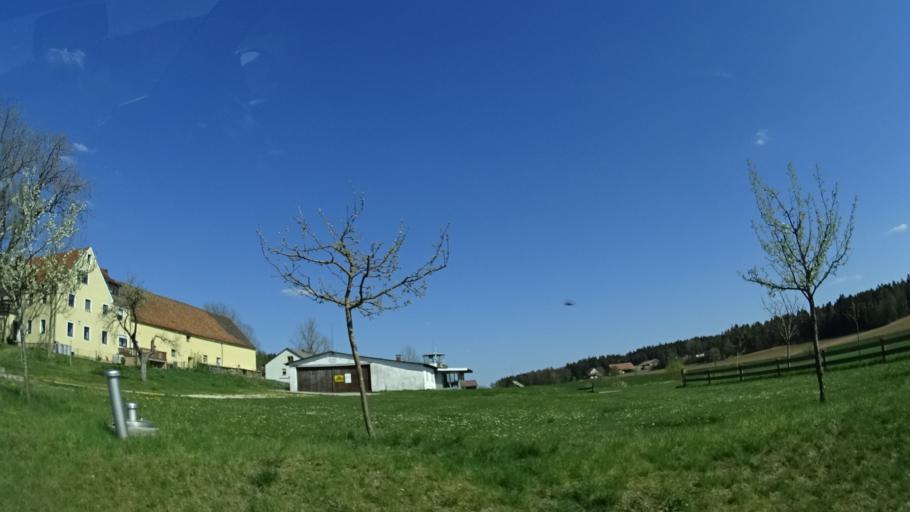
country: DE
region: Bavaria
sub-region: Upper Palatinate
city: Illschwang
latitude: 49.4986
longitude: 11.6545
